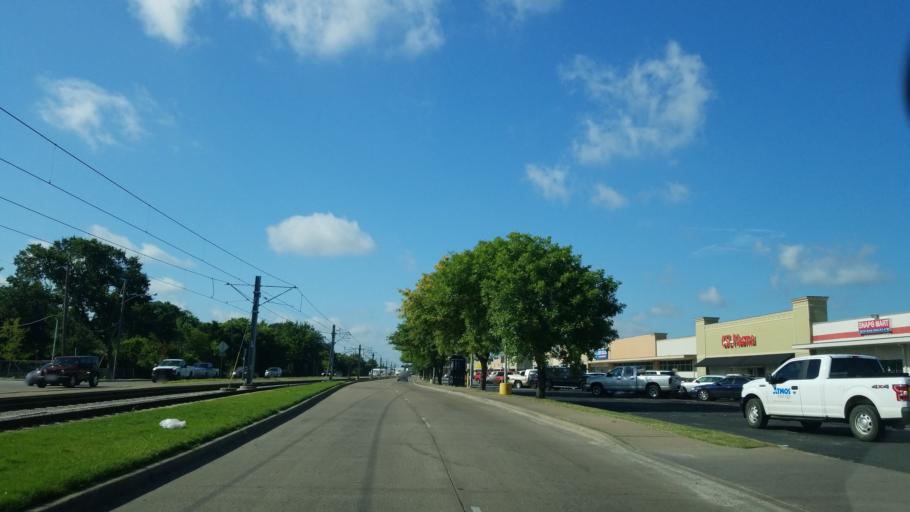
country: US
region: Texas
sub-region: Dallas County
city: Dallas
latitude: 32.7168
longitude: -96.8045
